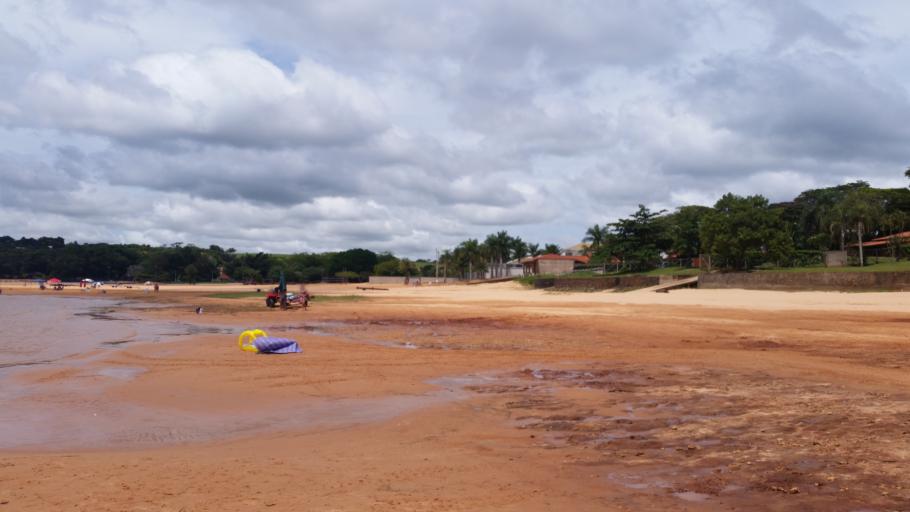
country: BR
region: Sao Paulo
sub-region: Itai
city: Itai
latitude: -23.2773
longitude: -49.0178
